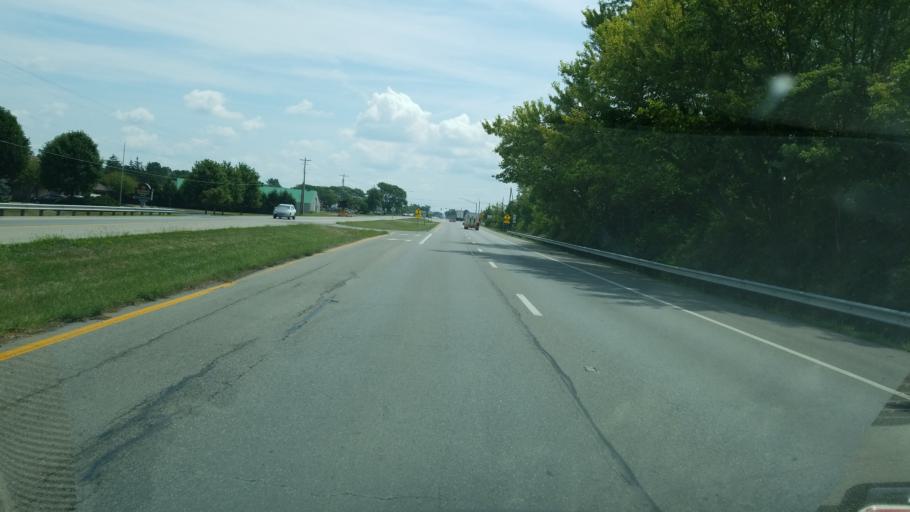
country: US
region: Ohio
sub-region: Delaware County
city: Delaware
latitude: 40.2965
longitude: -83.0427
